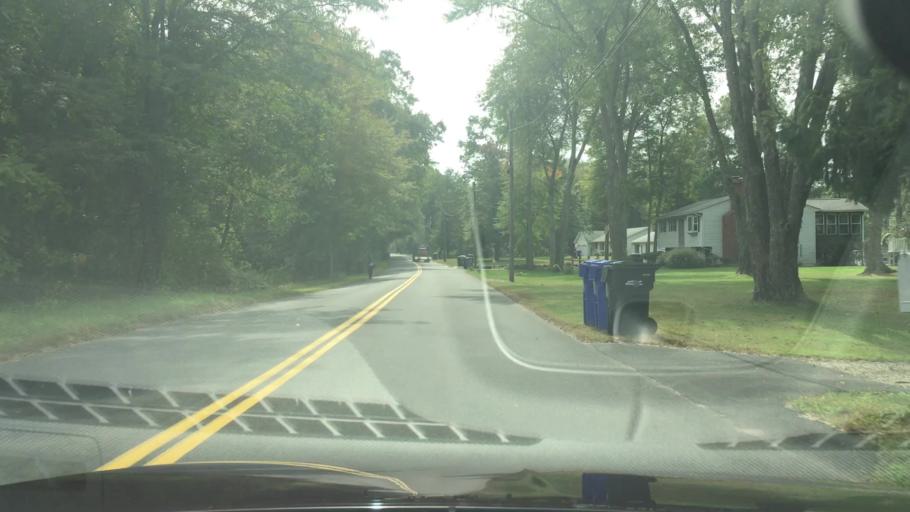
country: US
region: Connecticut
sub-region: Tolland County
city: Ellington
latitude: 41.9449
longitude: -72.4809
